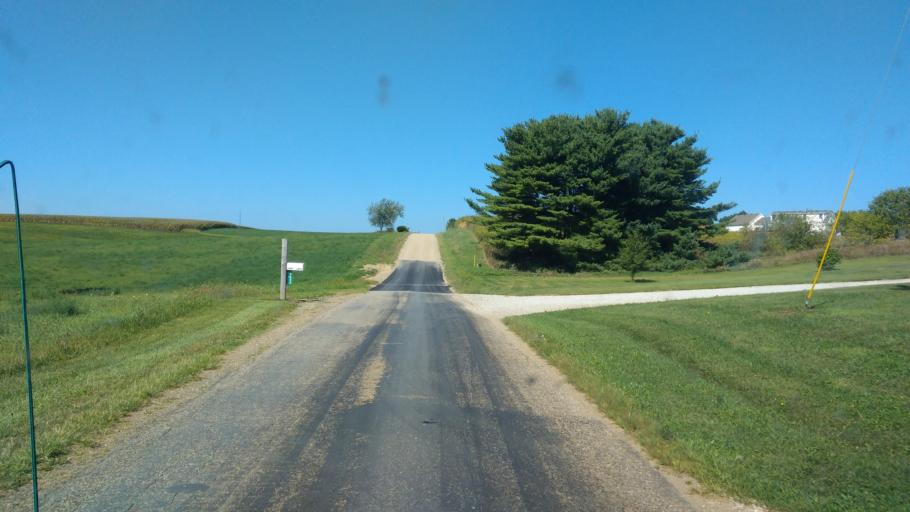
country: US
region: Ohio
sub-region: Knox County
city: Fredericktown
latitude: 40.4880
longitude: -82.4387
